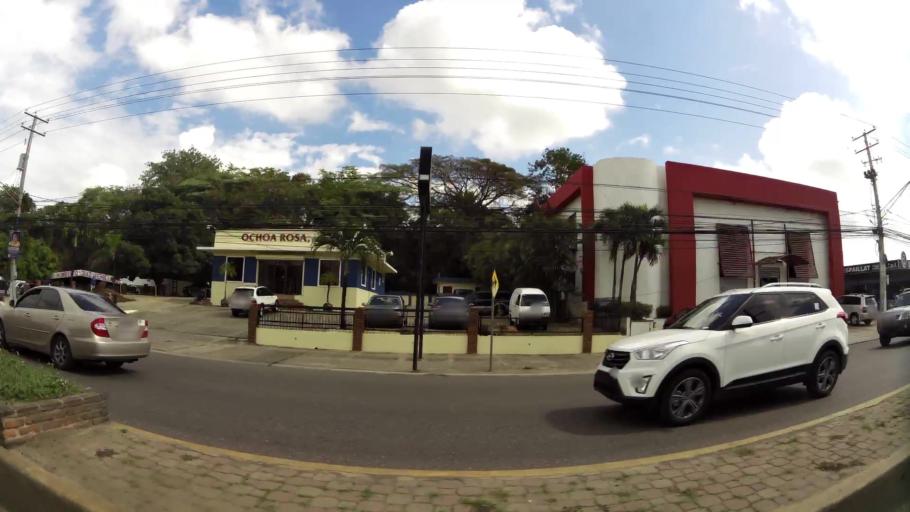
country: DO
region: Santiago
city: Santiago de los Caballeros
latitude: 19.4769
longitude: -70.6982
